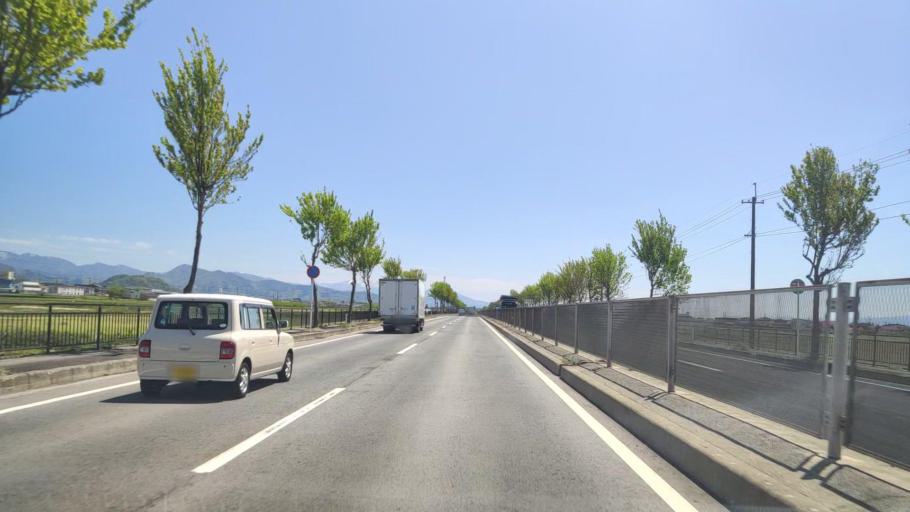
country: JP
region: Yamagata
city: Higashine
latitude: 38.4661
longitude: 140.3826
